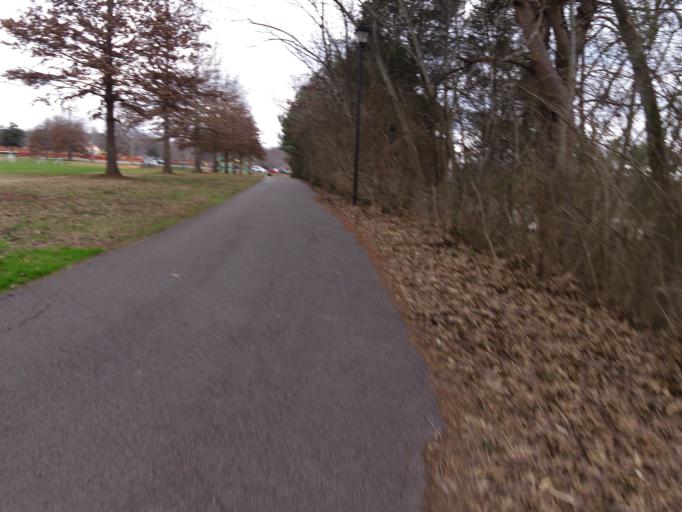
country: US
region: Tennessee
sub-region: Knox County
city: Knoxville
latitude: 35.9173
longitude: -83.9894
